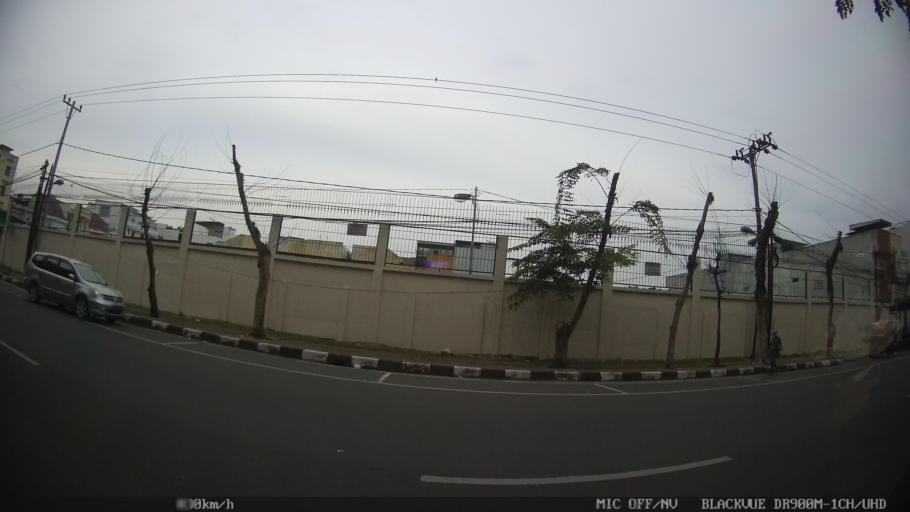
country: ID
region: North Sumatra
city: Medan
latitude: 3.5991
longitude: 98.6886
